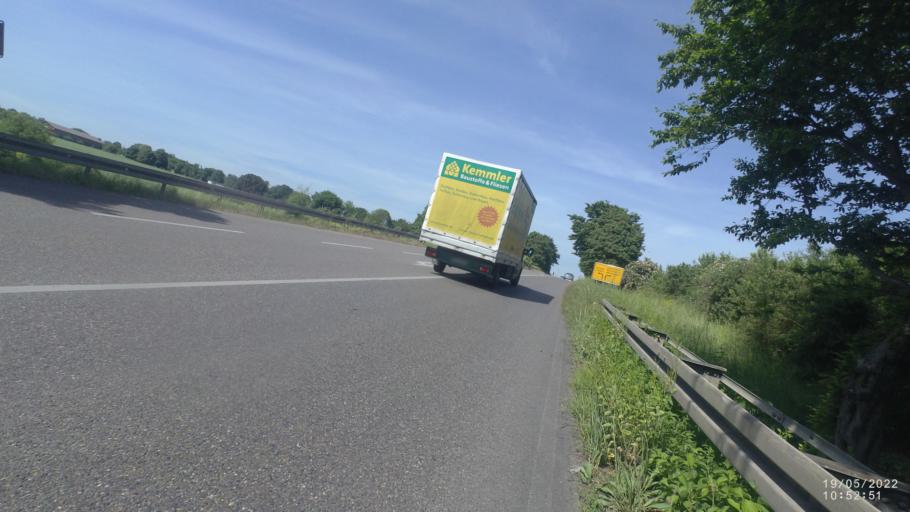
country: DE
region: Baden-Wuerttemberg
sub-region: Regierungsbezirk Stuttgart
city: Stuttgart Muehlhausen
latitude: 48.8383
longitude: 9.2543
